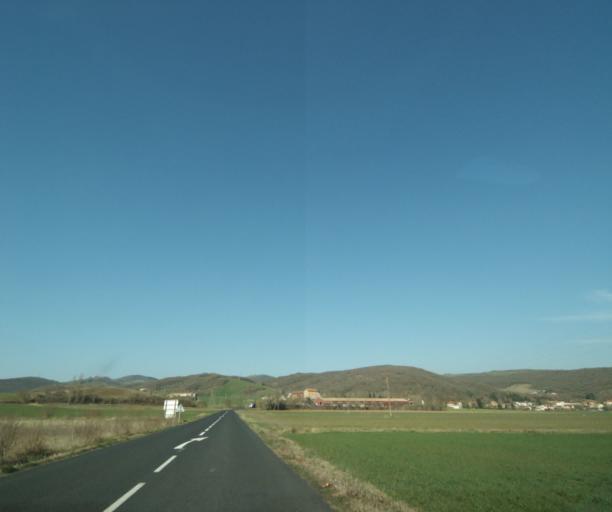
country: FR
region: Midi-Pyrenees
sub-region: Departement de l'Aveyron
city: Camares
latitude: 43.8845
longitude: 2.8173
